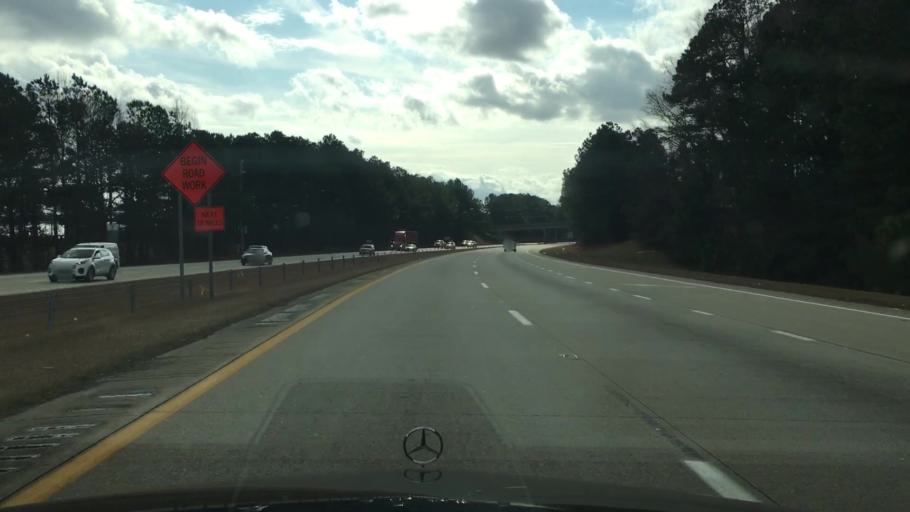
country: US
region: North Carolina
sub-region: Johnston County
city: Clayton
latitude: 35.6009
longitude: -78.5638
